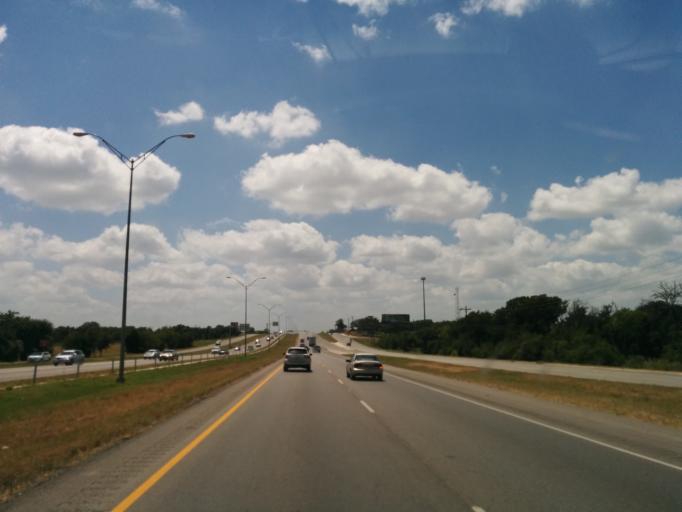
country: US
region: Texas
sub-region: Bastrop County
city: Bastrop
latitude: 30.1112
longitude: -97.3607
